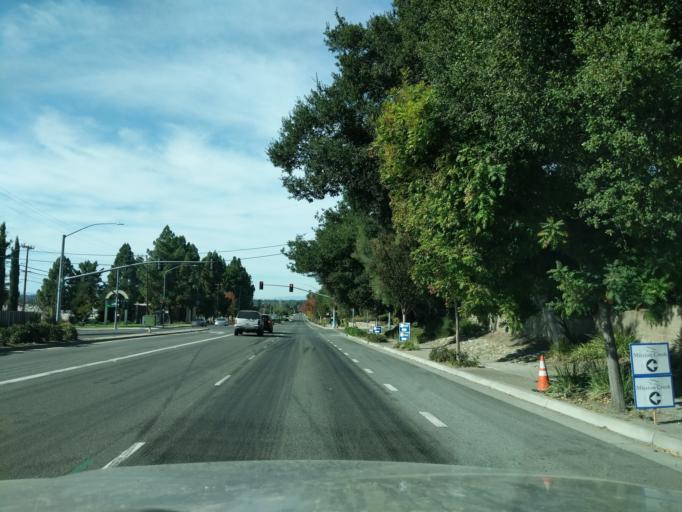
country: US
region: California
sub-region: Alameda County
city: Fremont
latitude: 37.5448
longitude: -121.9311
